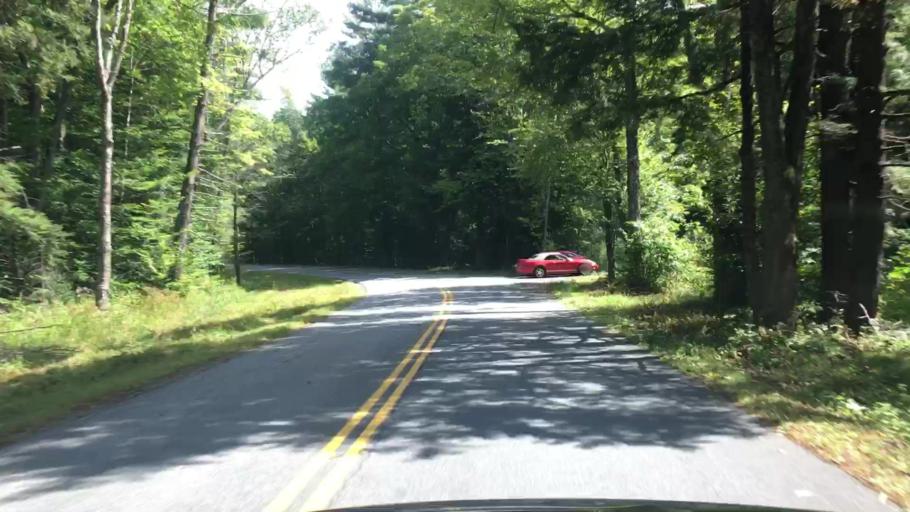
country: US
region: Vermont
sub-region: Windham County
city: West Brattleboro
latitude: 42.8129
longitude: -72.7304
